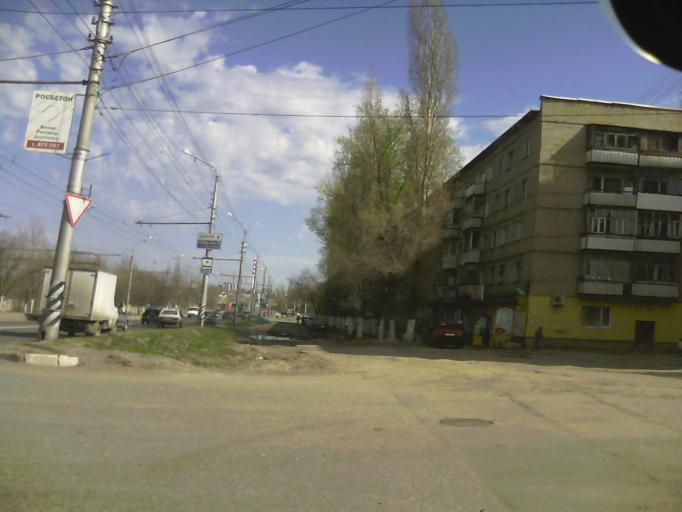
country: RU
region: Saratov
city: Sokolovyy
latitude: 51.5998
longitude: 45.9240
